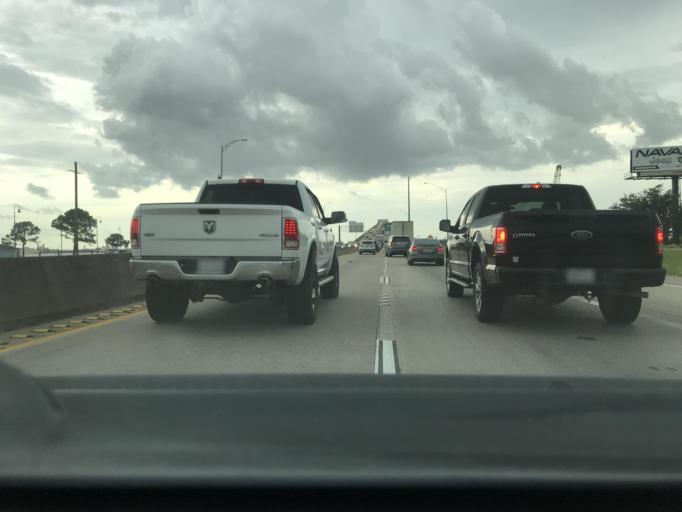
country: US
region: Louisiana
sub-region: Calcasieu Parish
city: Westlake
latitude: 30.2373
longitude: -93.2348
